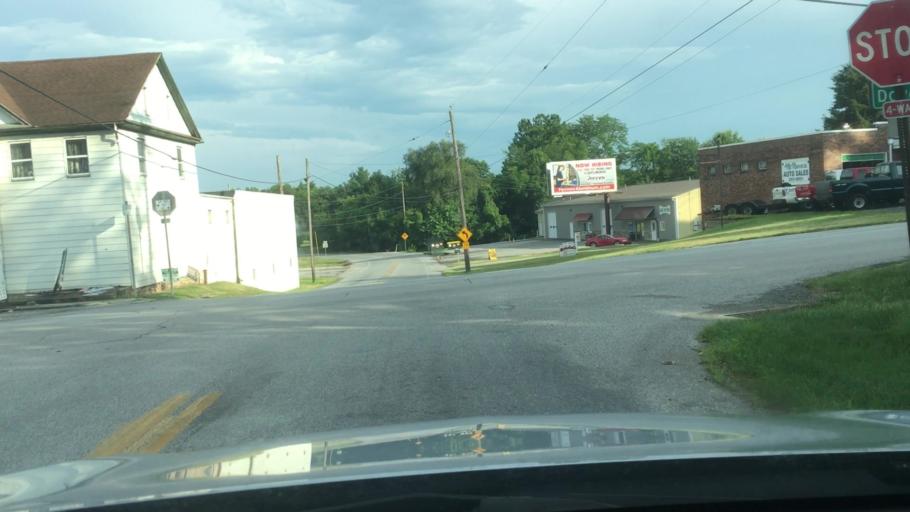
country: US
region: Pennsylvania
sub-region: York County
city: Weigelstown
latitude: 40.0169
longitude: -76.8141
